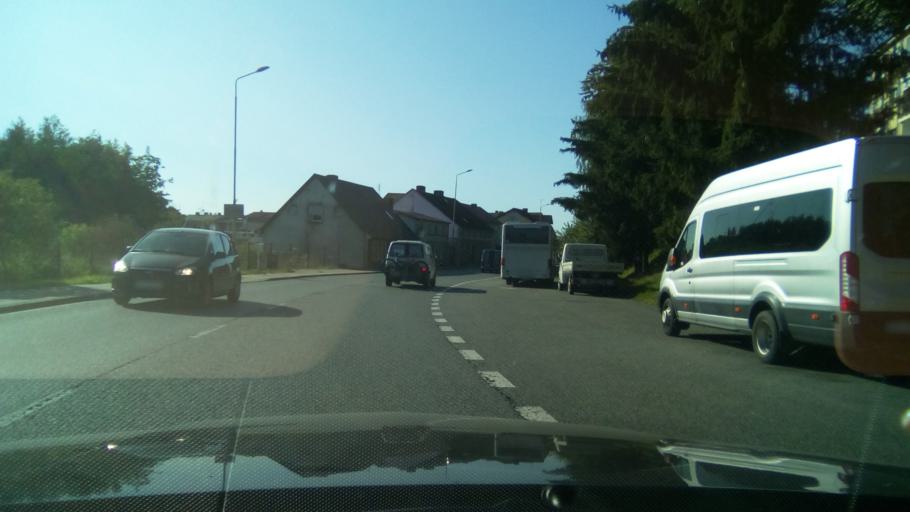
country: PL
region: West Pomeranian Voivodeship
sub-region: Powiat kamienski
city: Golczewo
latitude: 53.8238
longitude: 14.9827
